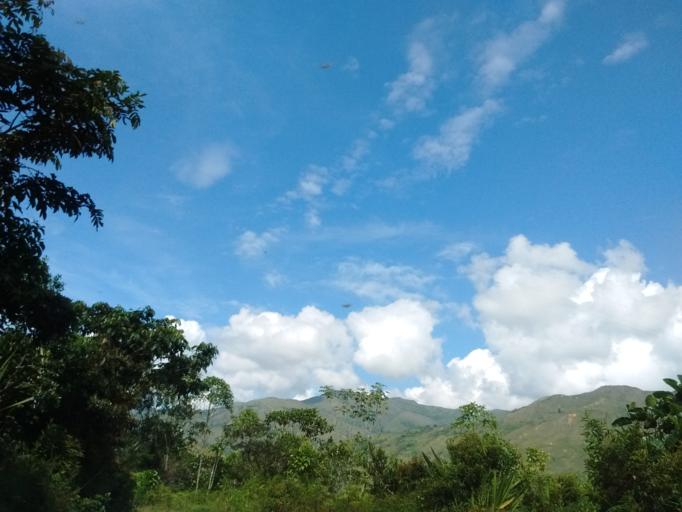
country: CO
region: Cauca
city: Morales
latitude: 2.6953
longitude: -76.7491
